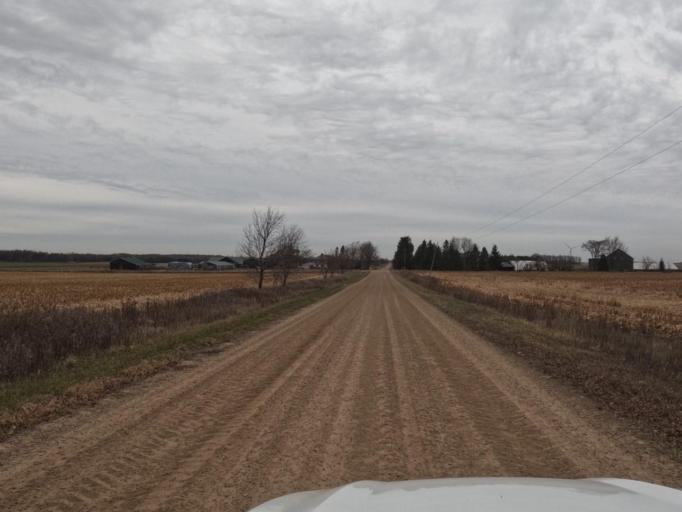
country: CA
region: Ontario
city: Shelburne
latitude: 44.0136
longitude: -80.3675
